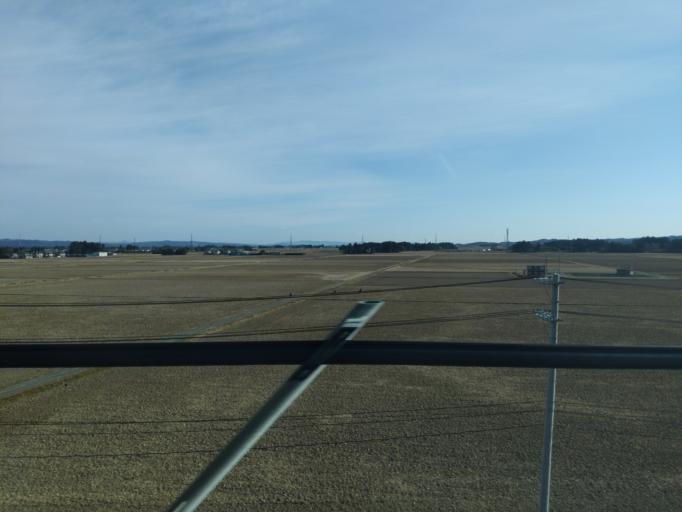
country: JP
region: Miyagi
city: Furukawa
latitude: 38.5499
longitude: 140.9624
